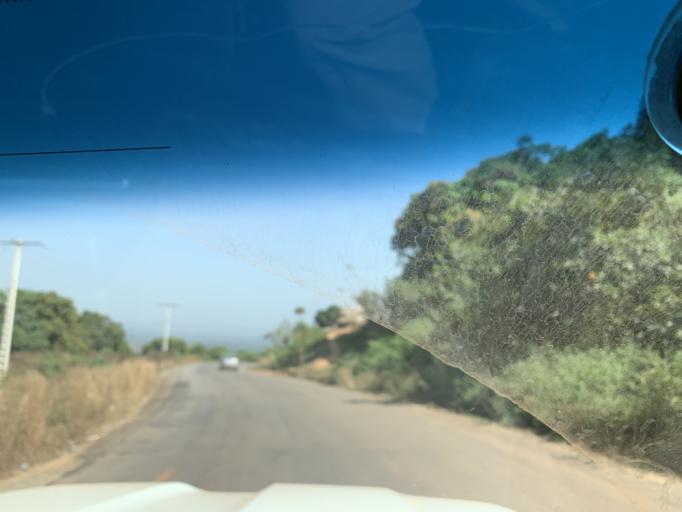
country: GN
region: Kindia
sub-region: Kindia
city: Kindia
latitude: 10.1781
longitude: -12.4782
